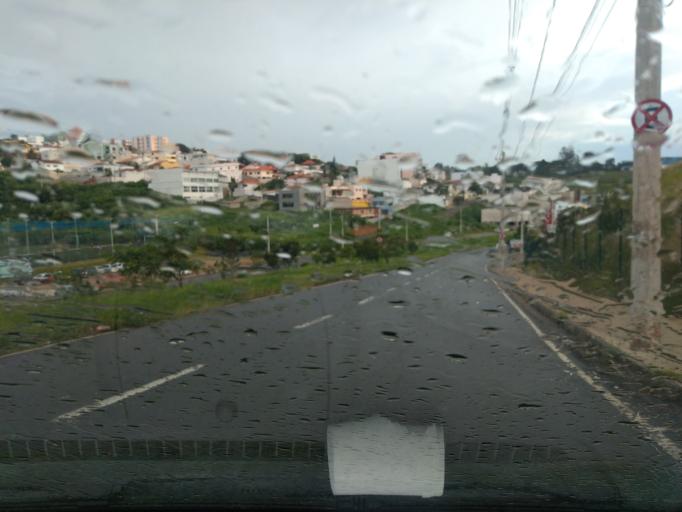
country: BR
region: Minas Gerais
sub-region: Varginha
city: Varginha
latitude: -21.5704
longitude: -45.4462
